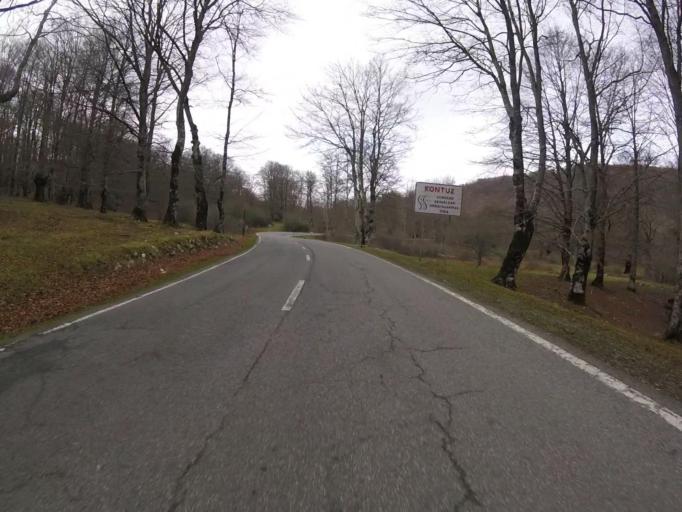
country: ES
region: Navarre
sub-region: Provincia de Navarra
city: Olazagutia
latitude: 42.8580
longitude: -2.1719
